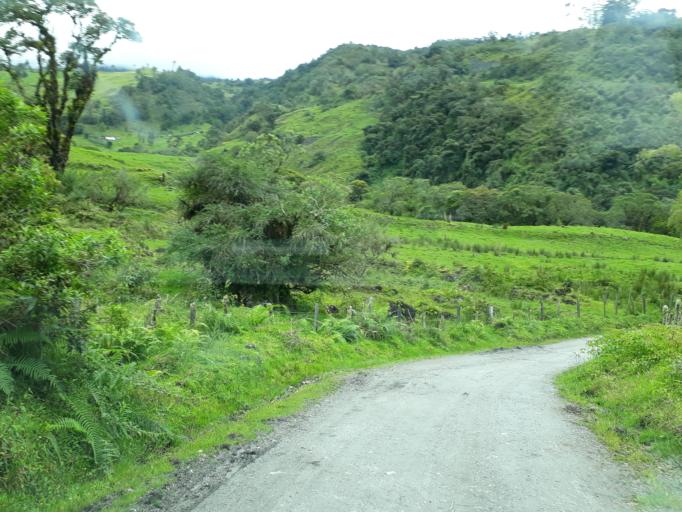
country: CO
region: Cundinamarca
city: Junin
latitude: 4.6775
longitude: -73.6810
